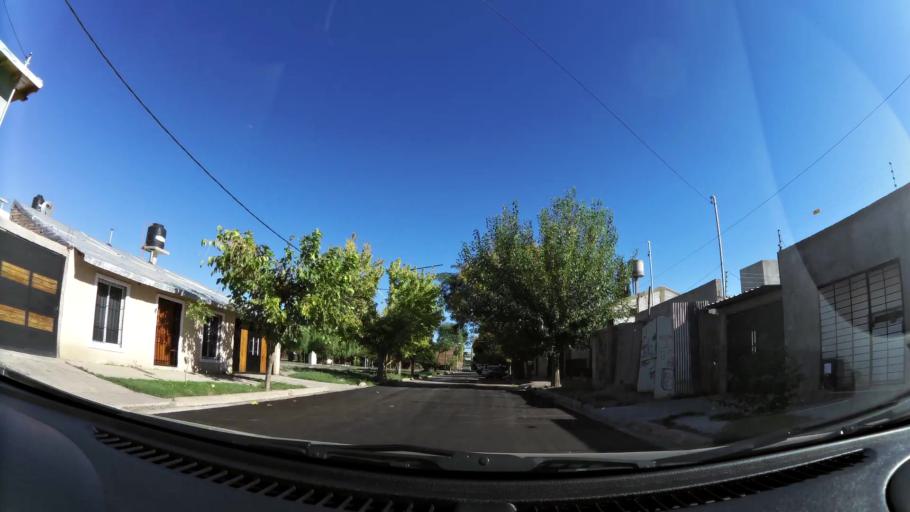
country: AR
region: Mendoza
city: Las Heras
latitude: -32.8493
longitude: -68.8294
